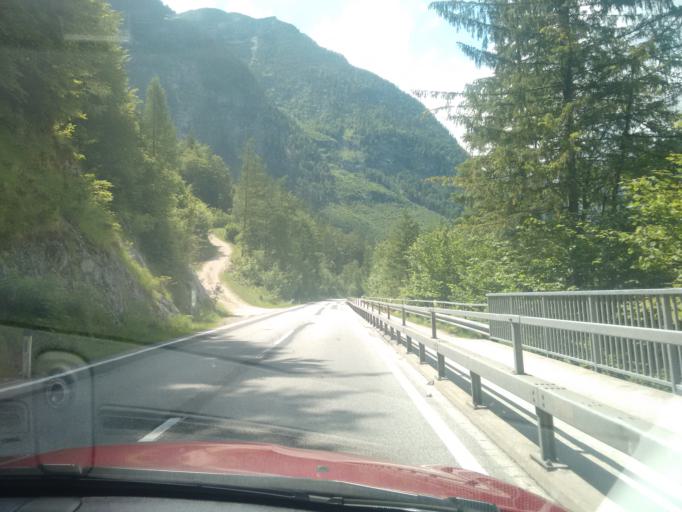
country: AT
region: Upper Austria
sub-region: Politischer Bezirk Gmunden
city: Bad Goisern
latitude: 47.5467
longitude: 13.6705
